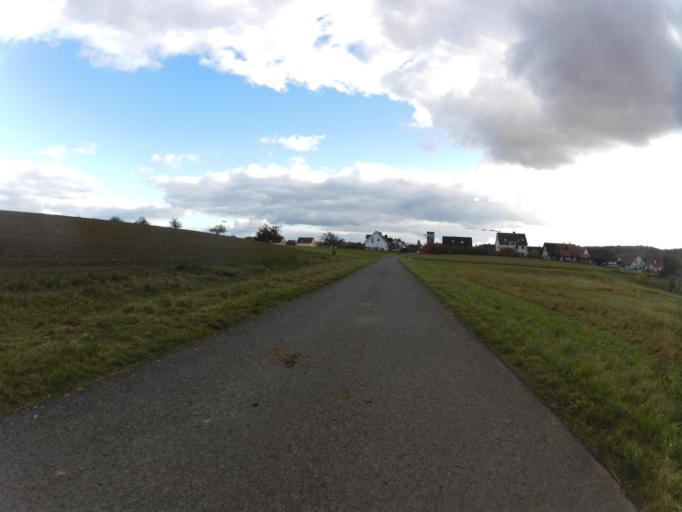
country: DE
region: Bavaria
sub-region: Regierungsbezirk Unterfranken
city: Kurnach
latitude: 49.8616
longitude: 10.0078
